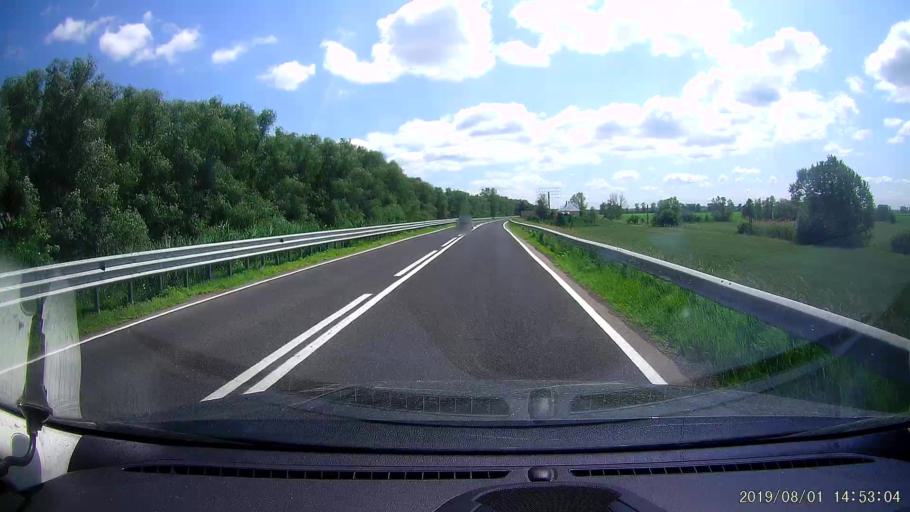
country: RO
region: Braila
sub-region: Comuna Vadeni
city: Vadeni
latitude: 45.3435
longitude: 28.0070
